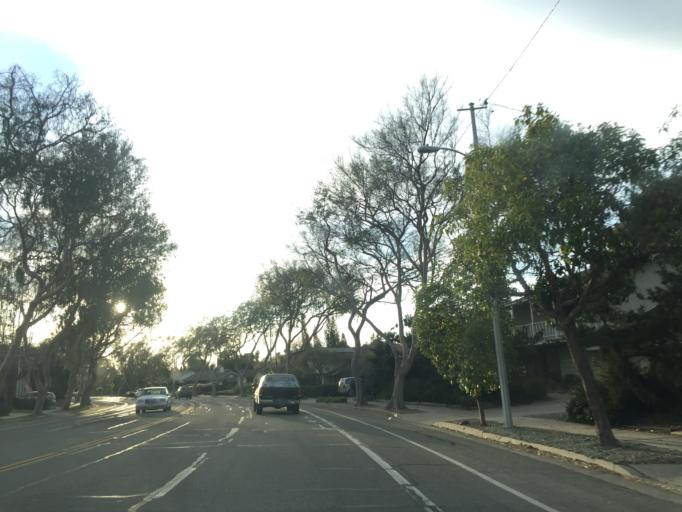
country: US
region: California
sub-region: Santa Barbara County
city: Goleta
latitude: 34.4532
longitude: -119.8160
